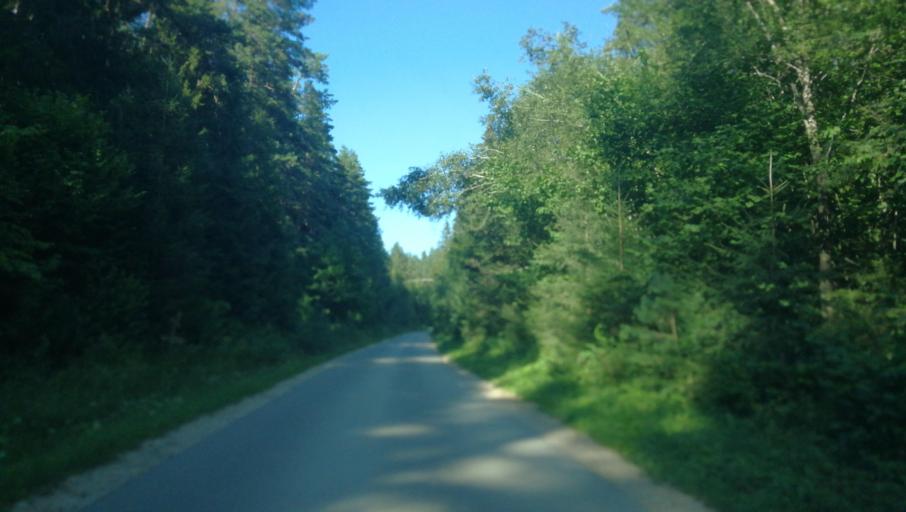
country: LV
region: Cesu Rajons
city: Cesis
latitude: 57.2836
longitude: 25.2103
